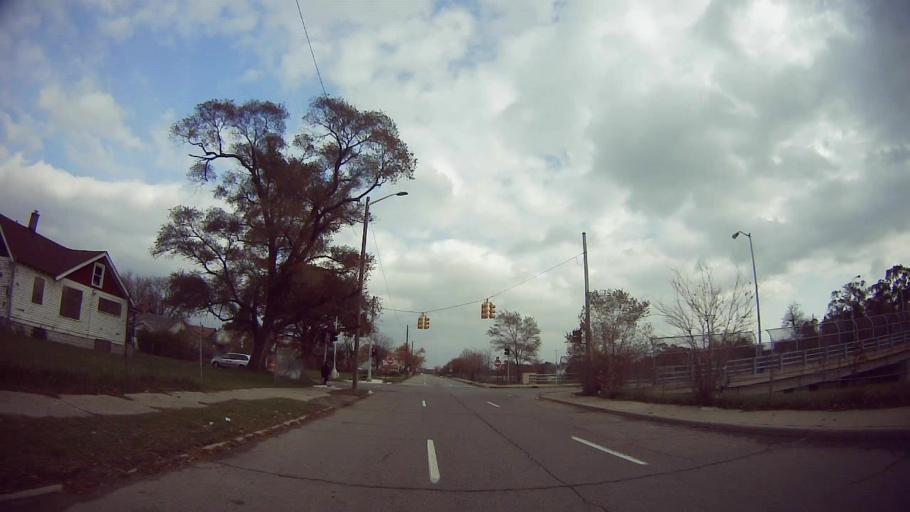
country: US
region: Michigan
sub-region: Wayne County
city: Highland Park
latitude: 42.4043
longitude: -83.1358
